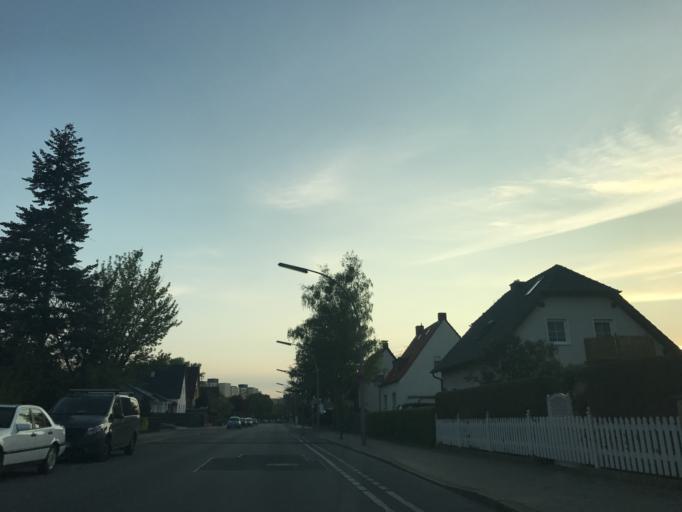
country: DE
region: Berlin
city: Wilhelmstadt
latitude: 52.5258
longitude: 13.1638
